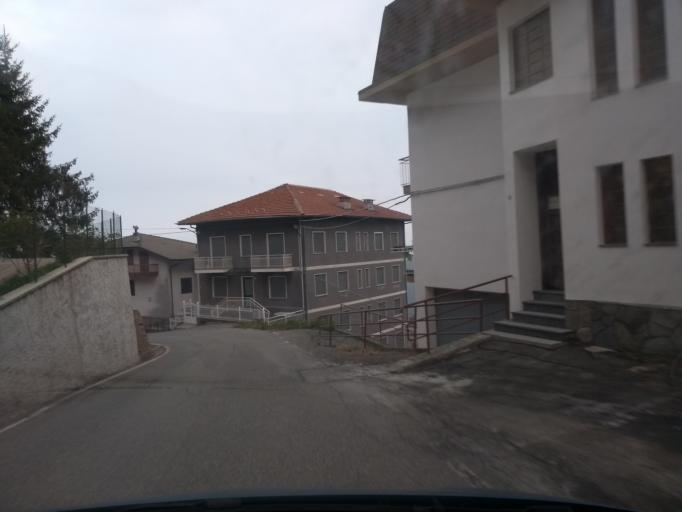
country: IT
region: Piedmont
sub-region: Provincia di Torino
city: Monastero di Lanzo
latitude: 45.3015
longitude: 7.4246
